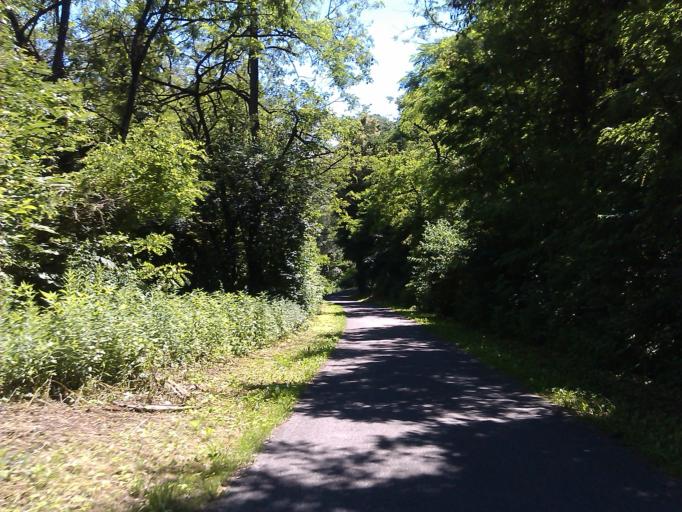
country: IT
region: Trentino-Alto Adige
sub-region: Bolzano
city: San Giacomo
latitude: 46.4461
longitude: 11.3086
